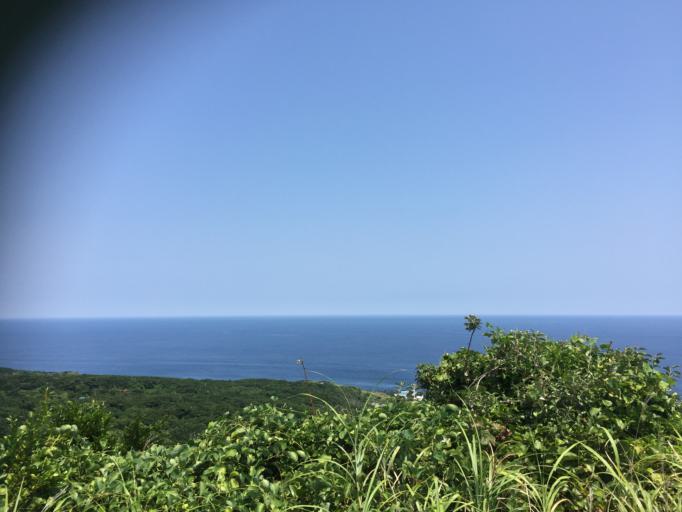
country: JP
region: Shizuoka
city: Shimoda
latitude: 34.1026
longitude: 139.5537
